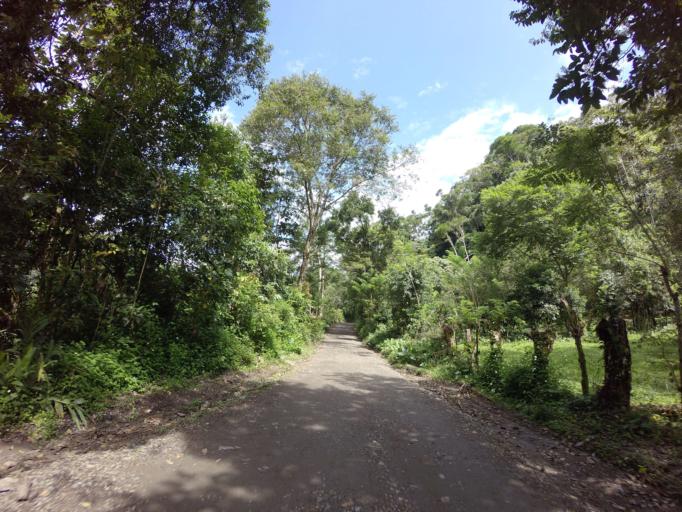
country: CO
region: Antioquia
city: Narino
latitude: 5.5391
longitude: -75.1298
